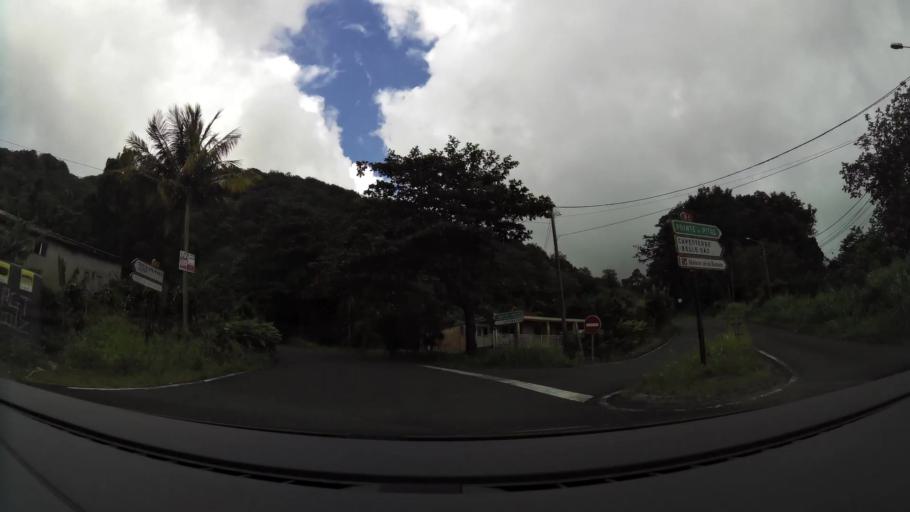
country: GP
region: Guadeloupe
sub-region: Guadeloupe
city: Trois-Rivieres
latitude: 15.9936
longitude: -61.6548
